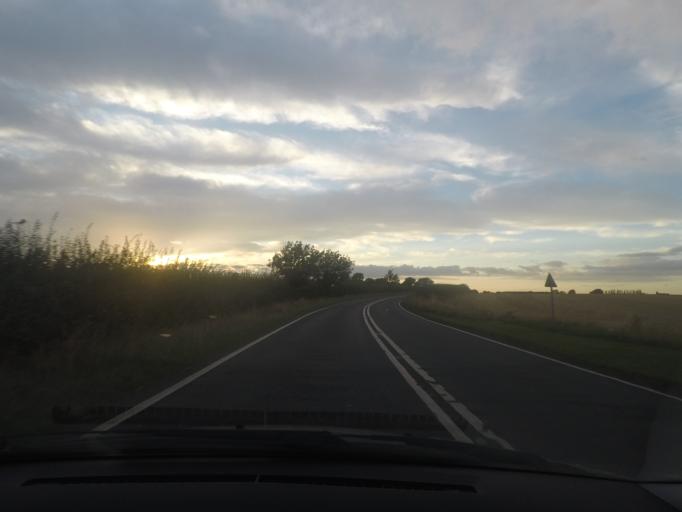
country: GB
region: England
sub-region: North East Lincolnshire
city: Laceby
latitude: 53.5260
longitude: -0.1667
